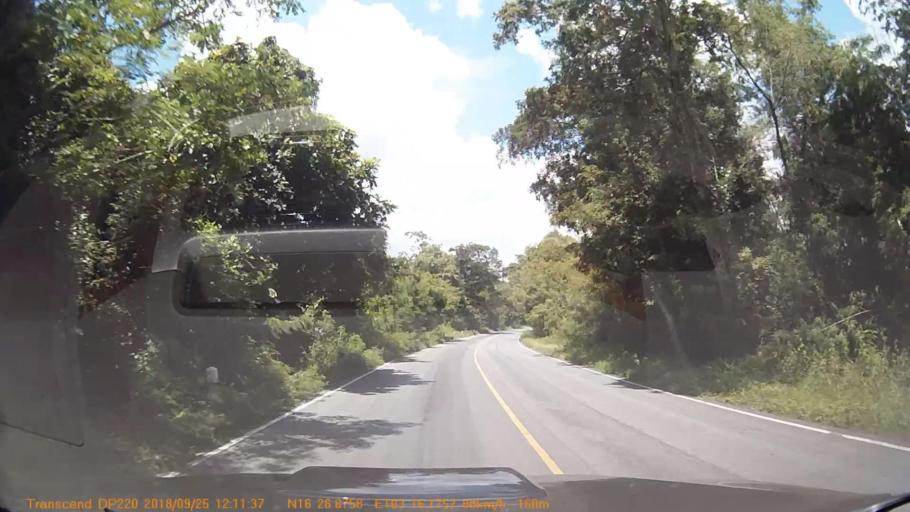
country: TH
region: Kalasin
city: Huai Mek
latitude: 16.4815
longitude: 103.2695
